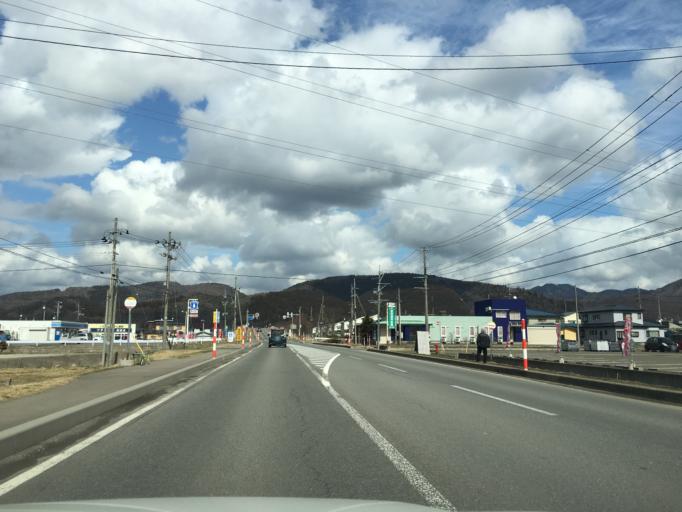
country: JP
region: Akita
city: Odate
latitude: 40.2205
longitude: 140.5869
